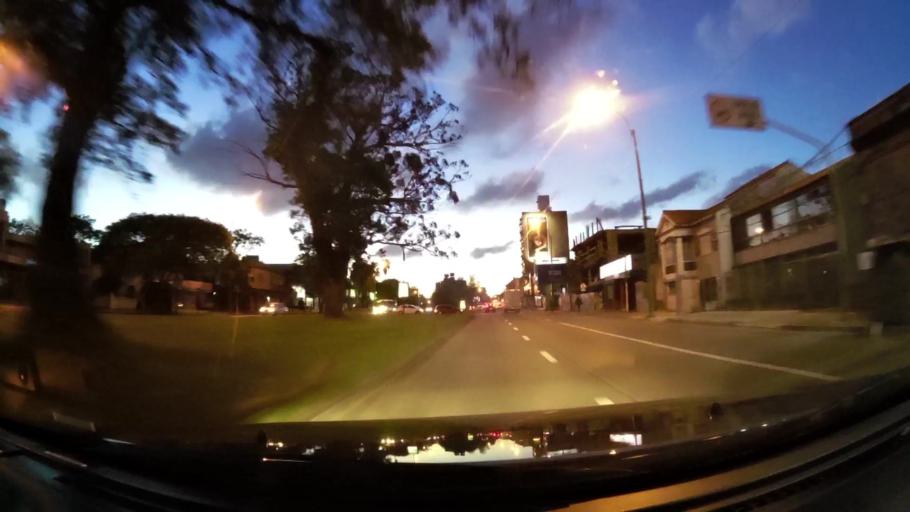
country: UY
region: Montevideo
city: Montevideo
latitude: -34.8865
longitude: -56.1394
